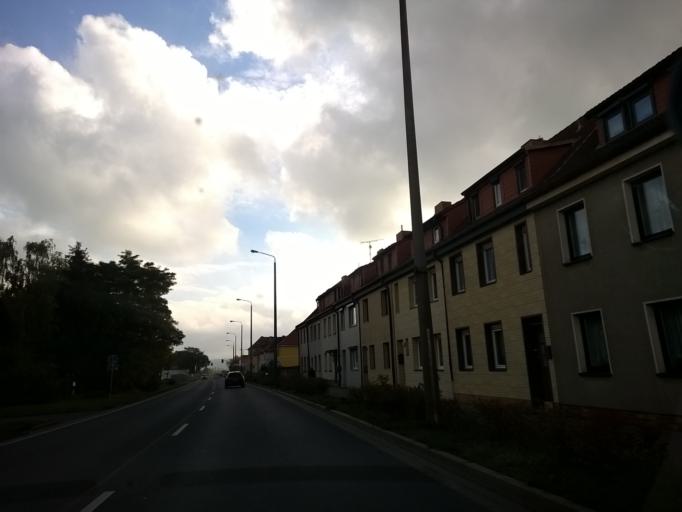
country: DE
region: Thuringia
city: Nordhausen
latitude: 51.4856
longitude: 10.8039
